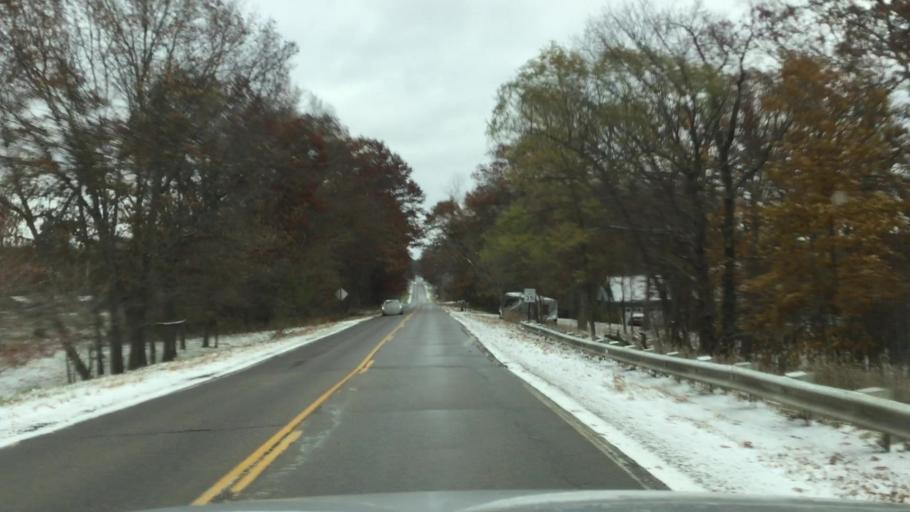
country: US
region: Michigan
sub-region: Livingston County
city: Brighton
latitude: 42.5377
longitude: -83.7487
